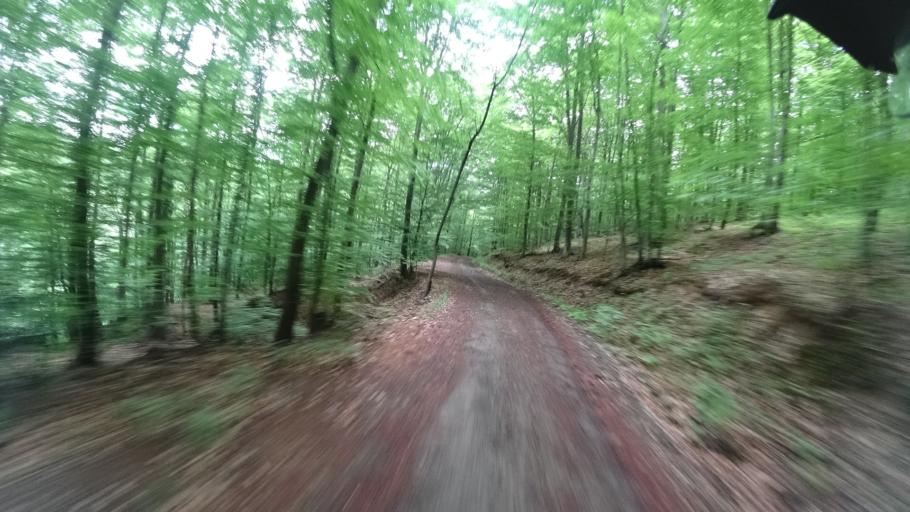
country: HR
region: Krapinsko-Zagorska
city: Oroslavje
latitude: 45.9351
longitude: 15.9303
